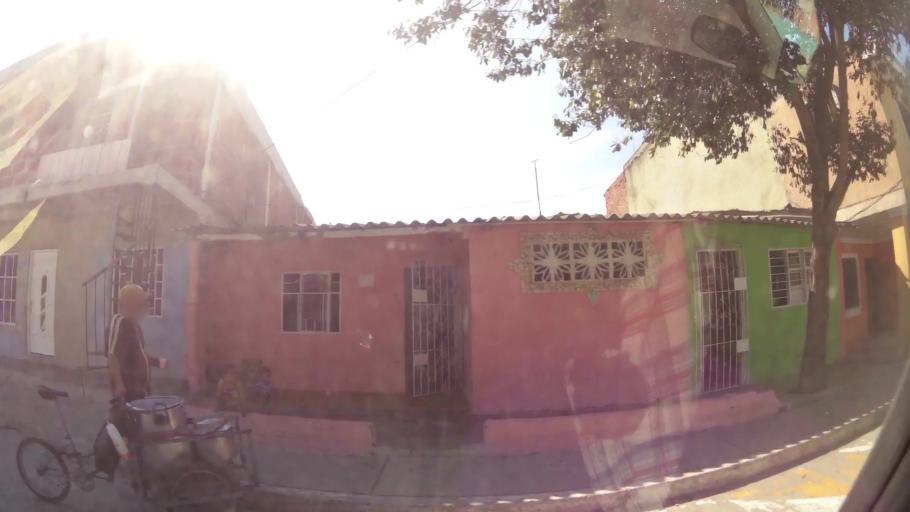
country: CO
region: Atlantico
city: Barranquilla
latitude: 10.9295
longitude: -74.8184
